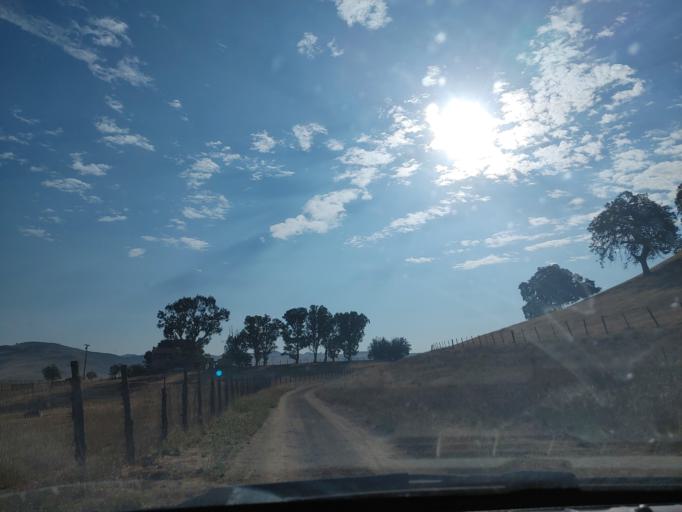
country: US
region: California
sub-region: San Benito County
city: Ridgemark
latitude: 36.7804
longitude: -121.2550
